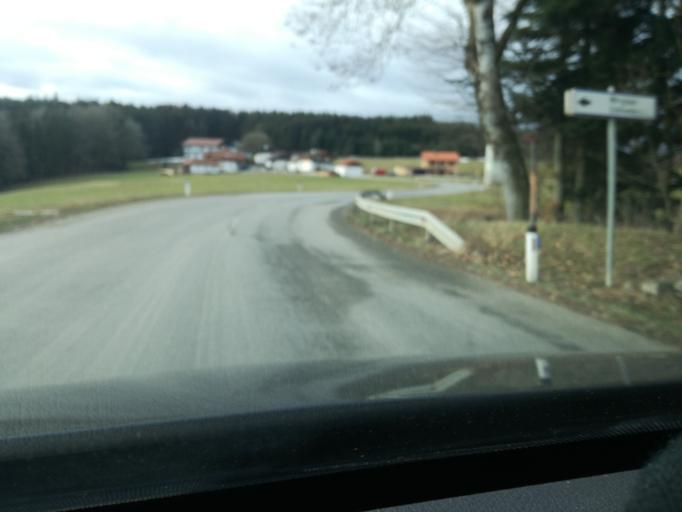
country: AT
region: Upper Austria
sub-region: Politischer Bezirk Ried im Innkreis
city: Waldzell
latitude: 48.1183
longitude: 13.4478
